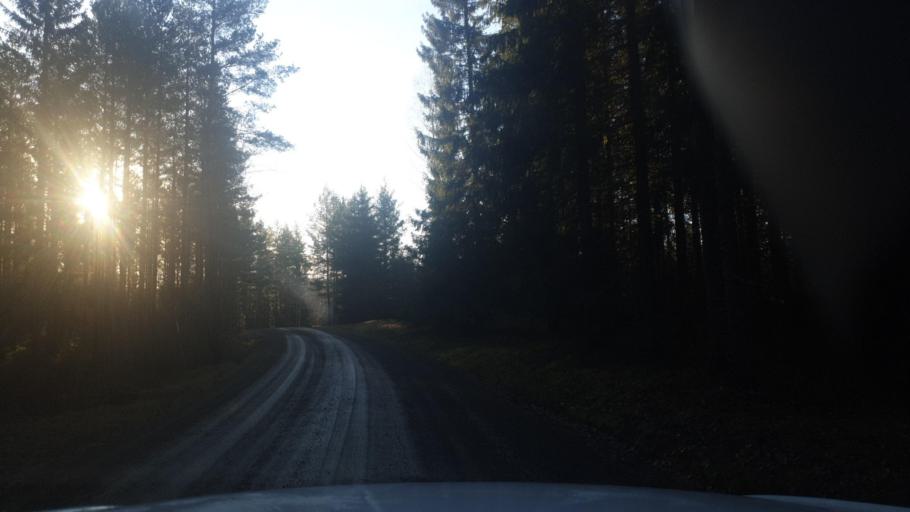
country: SE
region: Vaermland
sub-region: Karlstads Kommun
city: Edsvalla
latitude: 59.5809
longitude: 13.0728
